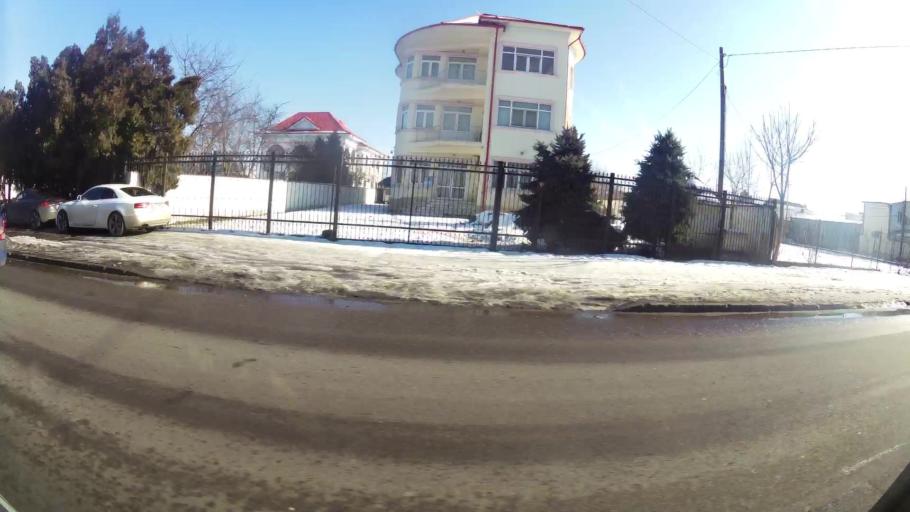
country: RO
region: Ilfov
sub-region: Comuna Magurele
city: Magurele
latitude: 44.3952
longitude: 26.0483
